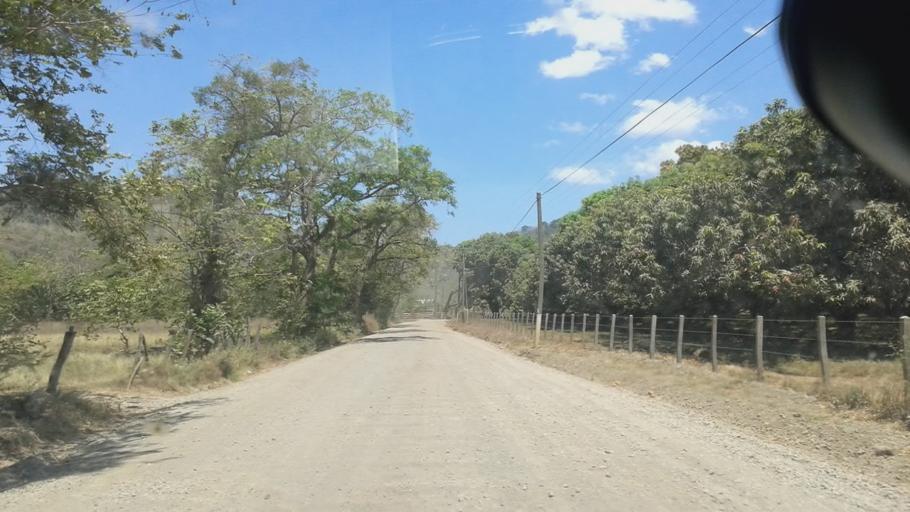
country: CR
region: Guanacaste
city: Samara
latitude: 9.9935
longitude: -85.6770
